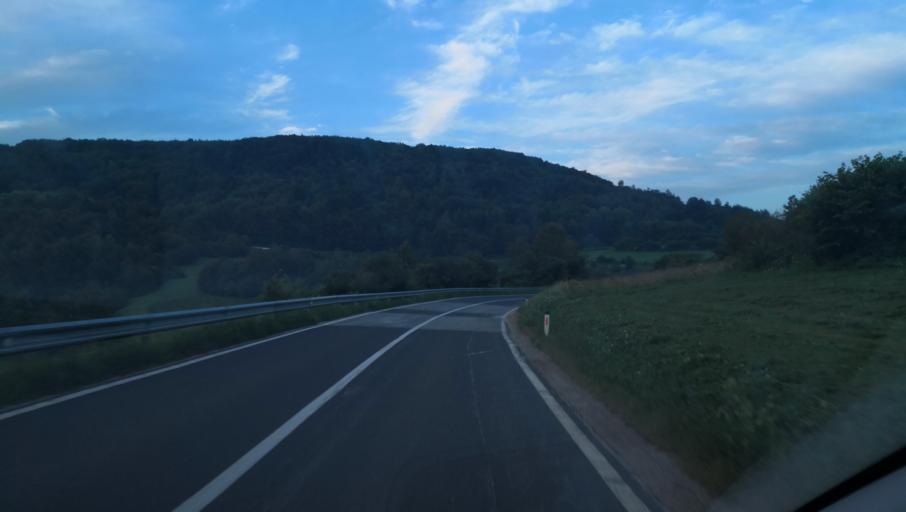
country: SI
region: Novo Mesto
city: Novo Mesto
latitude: 45.7393
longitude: 15.2228
